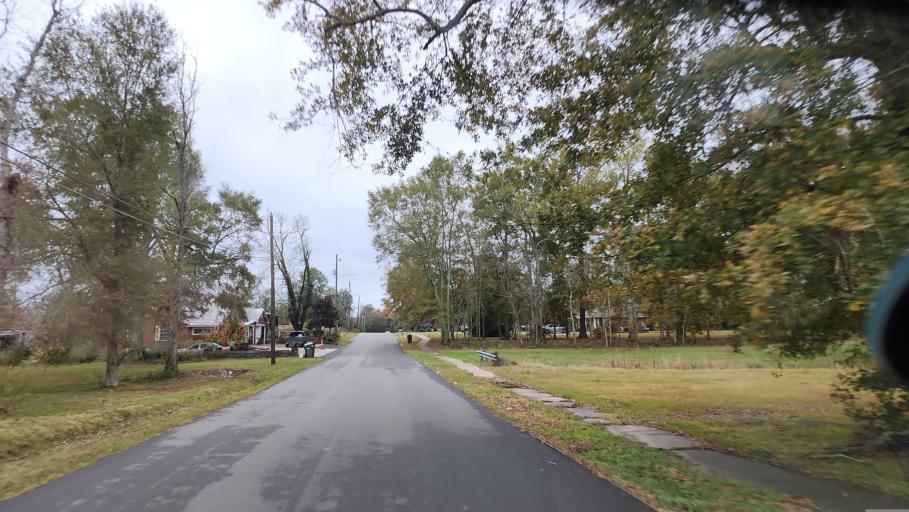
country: US
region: Mississippi
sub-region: Forrest County
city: Hattiesburg
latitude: 31.3016
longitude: -89.3036
